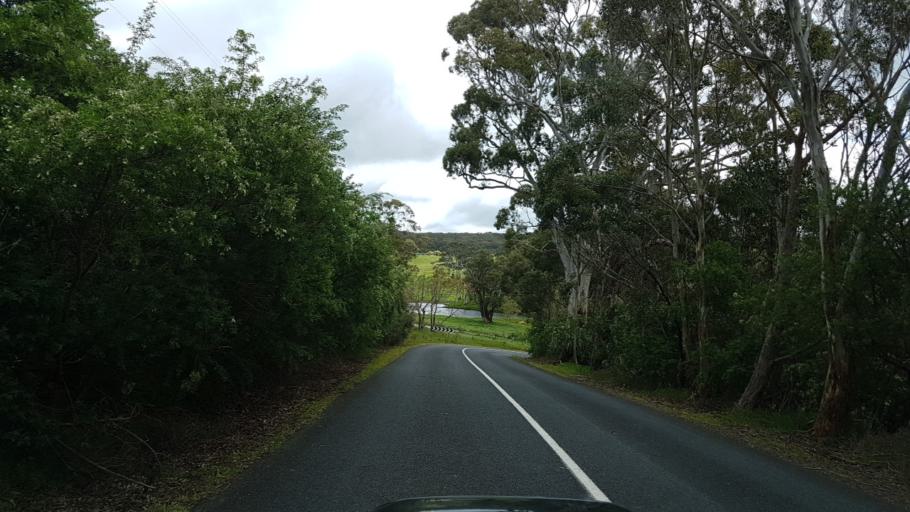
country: AU
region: South Australia
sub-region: Adelaide Hills
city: Lobethal
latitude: -34.8894
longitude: 138.8909
